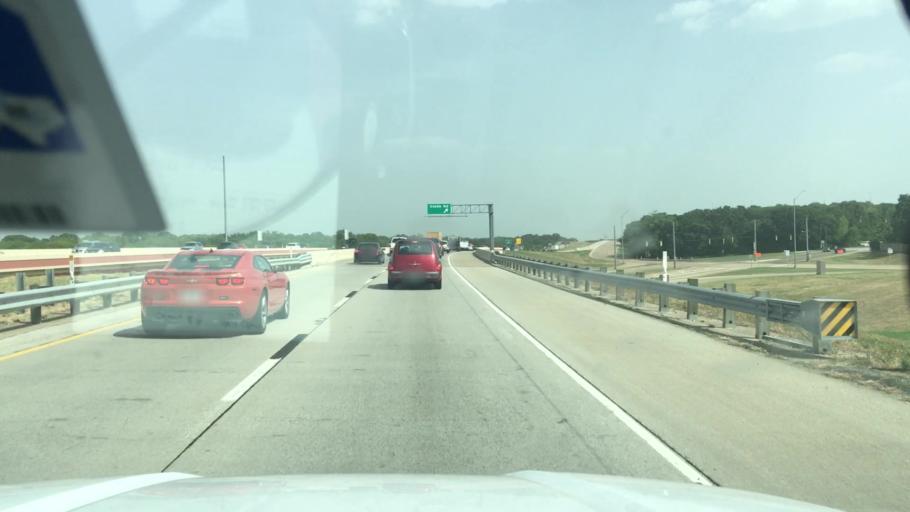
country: US
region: Texas
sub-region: Tarrant County
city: Grapevine
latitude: 32.8926
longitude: -97.0831
